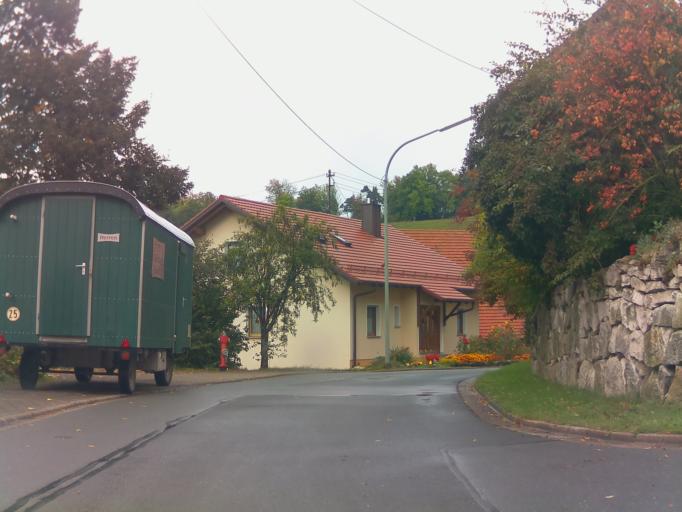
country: DE
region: Bavaria
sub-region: Upper Franconia
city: Schesslitz
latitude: 50.0155
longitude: 11.0254
